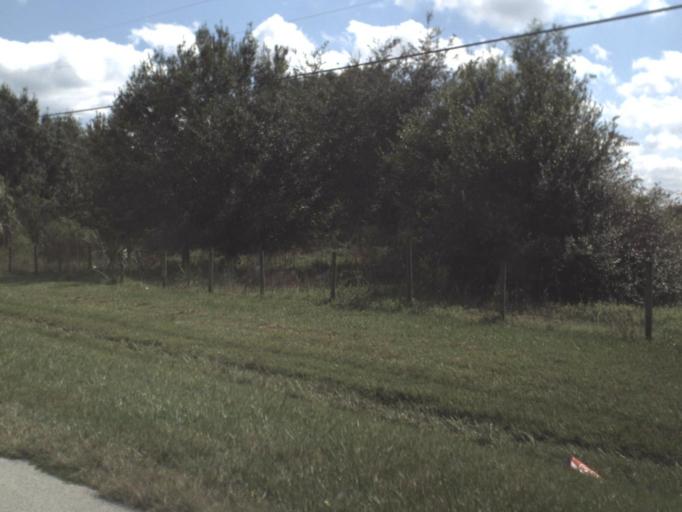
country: US
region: Florida
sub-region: Hardee County
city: Zolfo Springs
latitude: 27.4929
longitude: -81.7818
